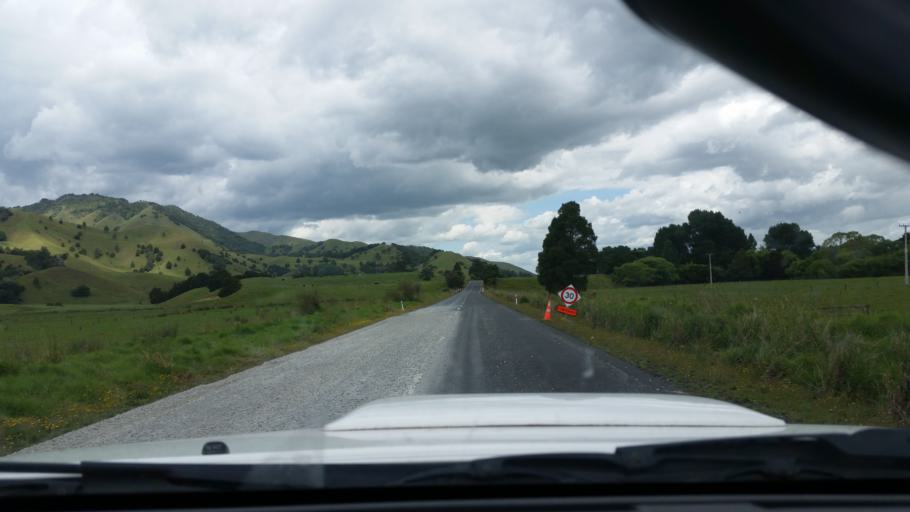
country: NZ
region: Northland
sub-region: Kaipara District
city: Dargaville
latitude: -35.7898
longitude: 173.9127
